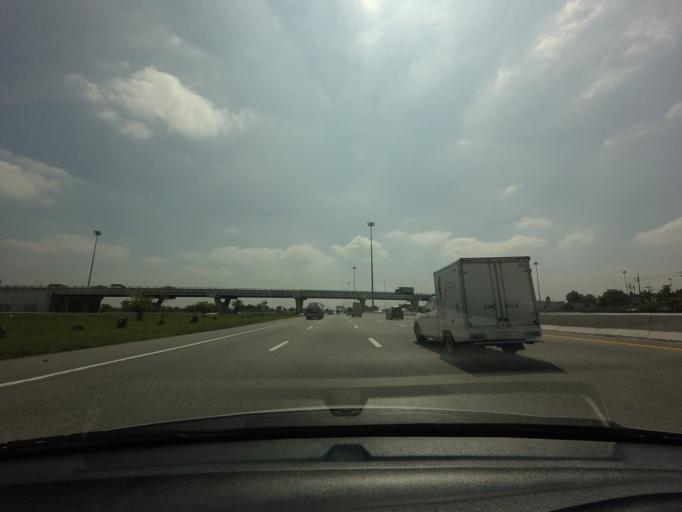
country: TH
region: Chachoengsao
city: Bang Pakong
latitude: 13.5999
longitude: 100.9531
